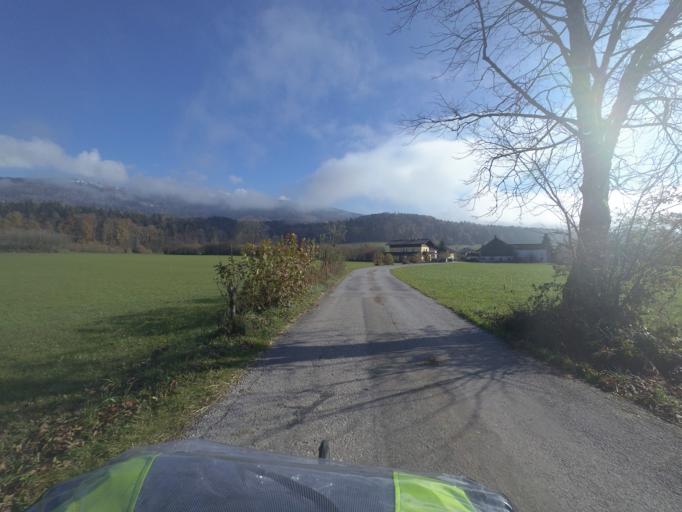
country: AT
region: Salzburg
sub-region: Politischer Bezirk Hallein
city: Adnet
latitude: 47.6848
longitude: 13.1415
